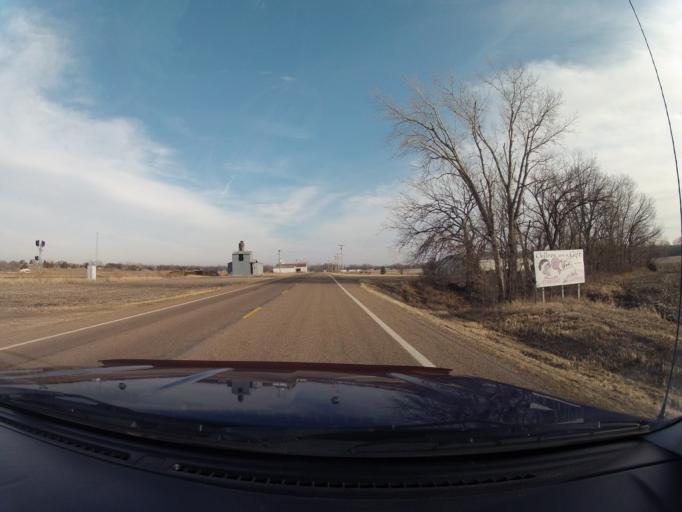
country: US
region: Kansas
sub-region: Pottawatomie County
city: Saint Marys
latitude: 39.2006
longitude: -96.0876
